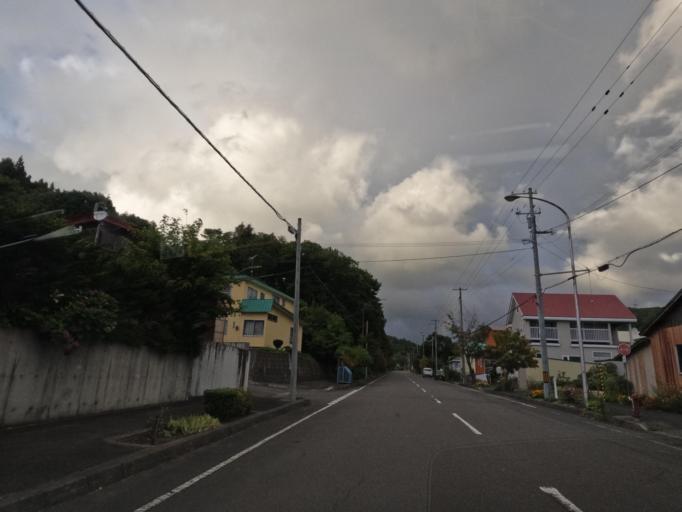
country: JP
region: Hokkaido
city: Muroran
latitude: 42.3718
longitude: 140.9556
